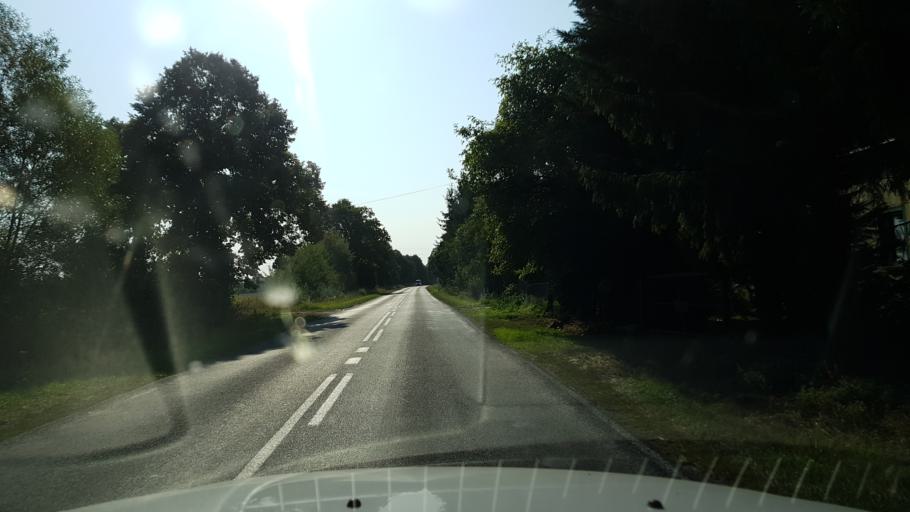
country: PL
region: West Pomeranian Voivodeship
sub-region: Powiat gryficki
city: Ploty
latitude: 53.7971
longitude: 15.2761
